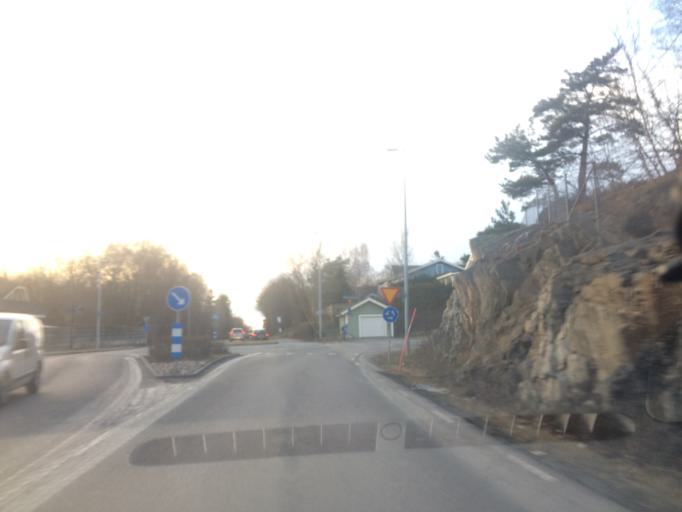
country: SE
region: Vaestra Goetaland
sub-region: Goteborg
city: Andalen
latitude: 57.7099
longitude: 11.7372
